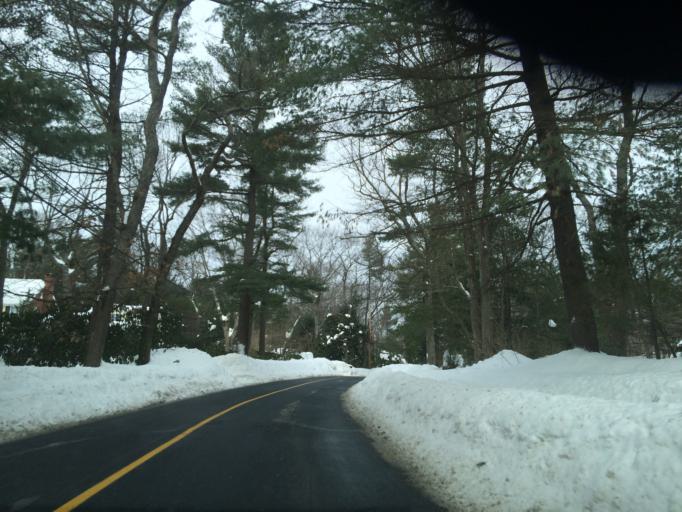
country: US
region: Massachusetts
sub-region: Middlesex County
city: Weston
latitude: 42.3440
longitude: -71.2974
